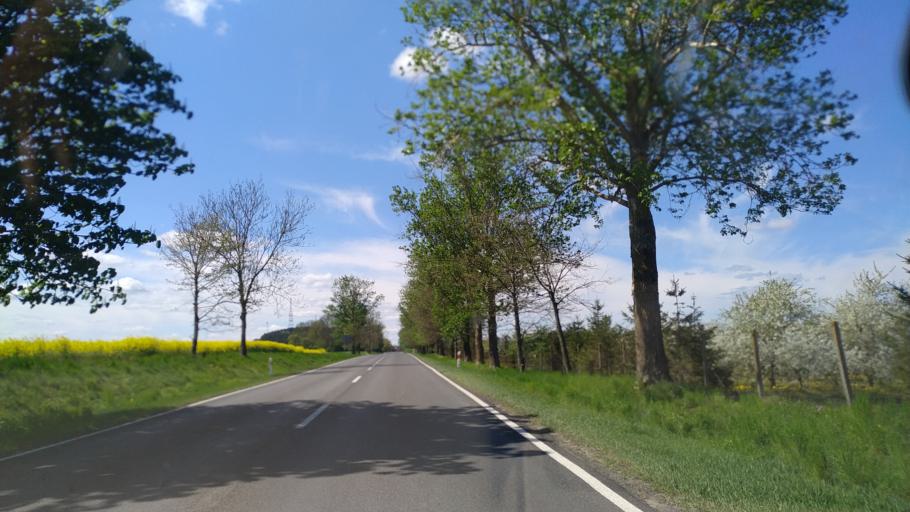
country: PL
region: Greater Poland Voivodeship
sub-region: Powiat pilski
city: Szydlowo
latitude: 53.2370
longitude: 16.6531
